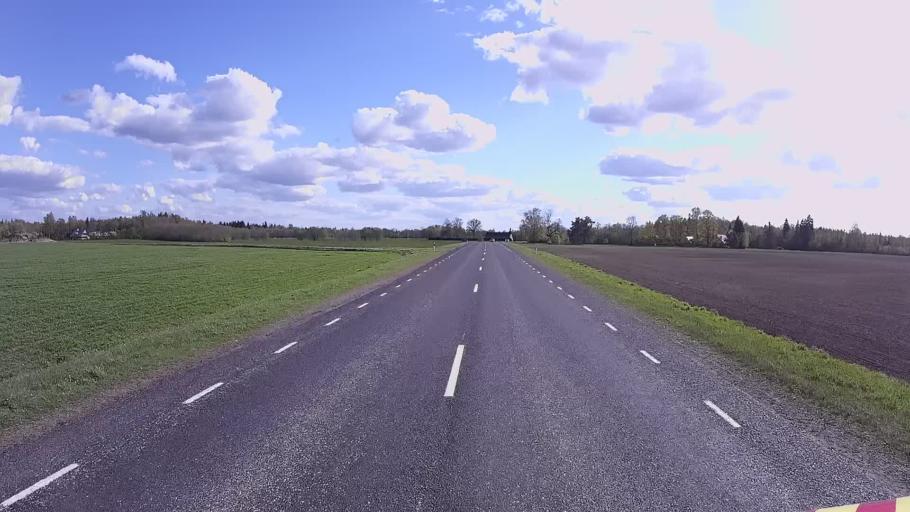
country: EE
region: Jogevamaa
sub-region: Jogeva linn
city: Jogeva
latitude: 58.7218
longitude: 26.1885
